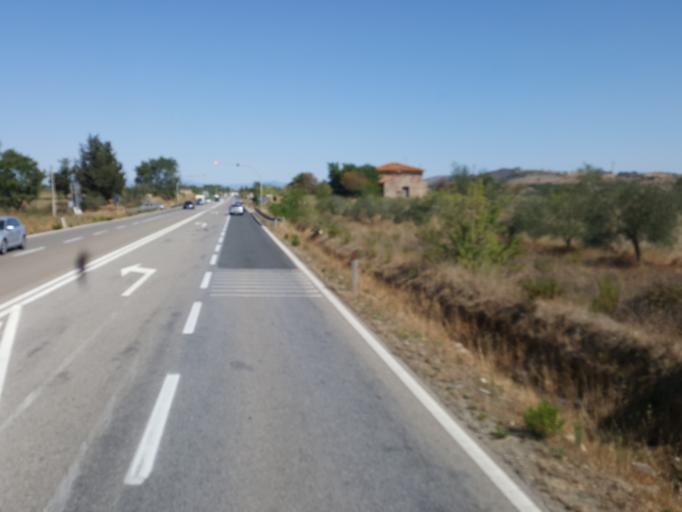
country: IT
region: Tuscany
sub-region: Provincia di Grosseto
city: Grosseto
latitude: 42.6772
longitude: 11.1409
